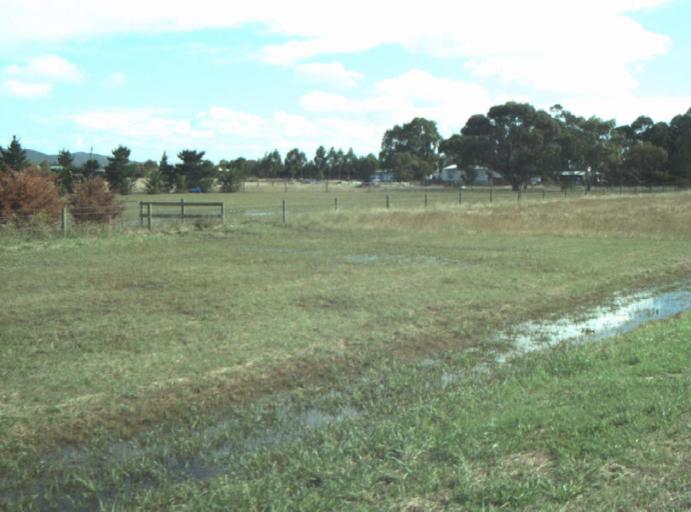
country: AU
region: Victoria
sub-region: Greater Geelong
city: Lara
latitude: -38.0170
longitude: 144.4480
